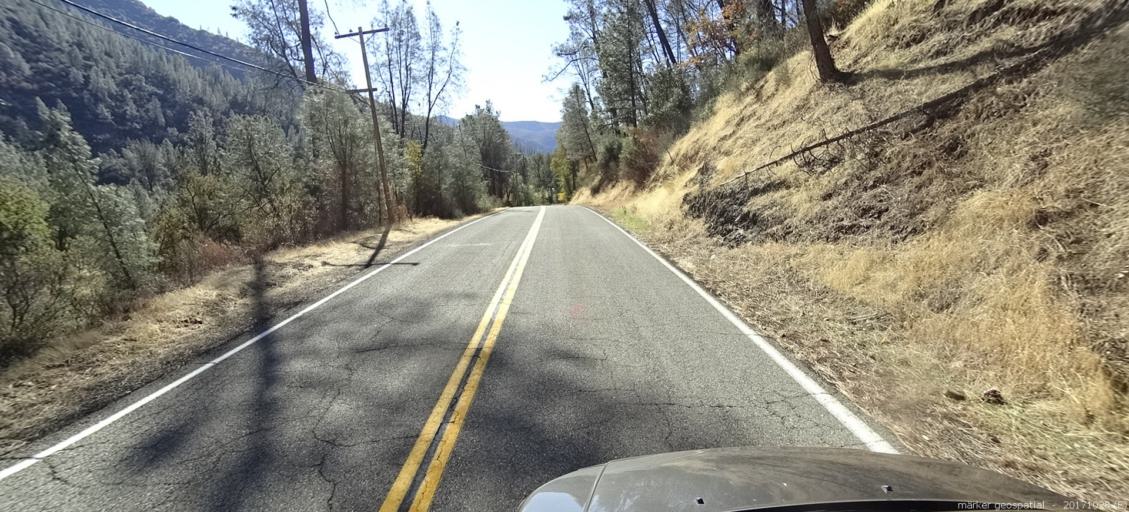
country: US
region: California
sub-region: Trinity County
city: Lewiston
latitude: 40.7442
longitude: -122.6257
